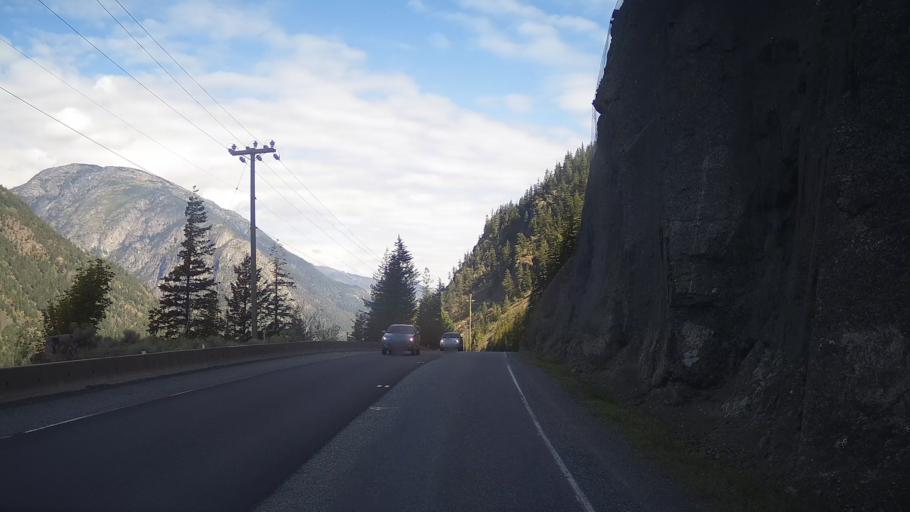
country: CA
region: British Columbia
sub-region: Thompson-Nicola Regional District
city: Ashcroft
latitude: 50.0789
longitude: -121.5508
